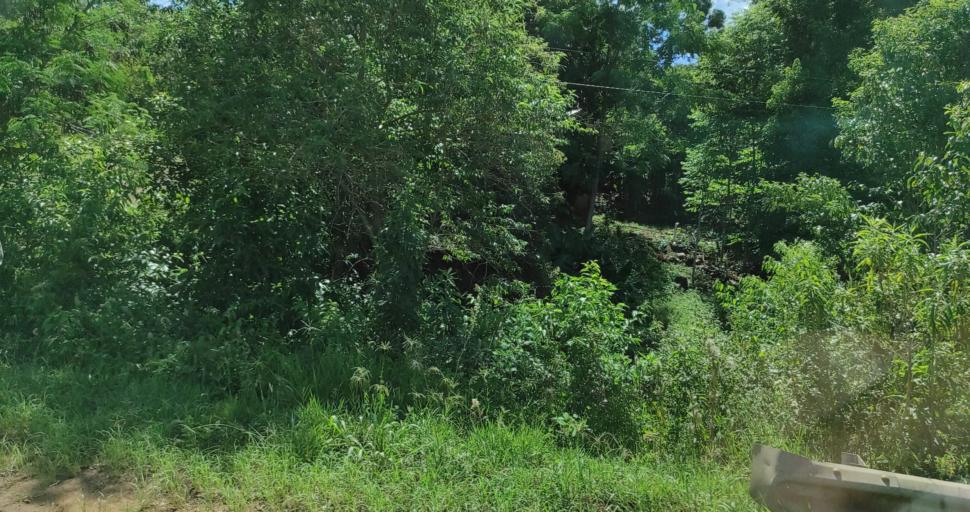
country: AR
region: Misiones
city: El Soberbio
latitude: -27.2779
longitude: -54.1965
